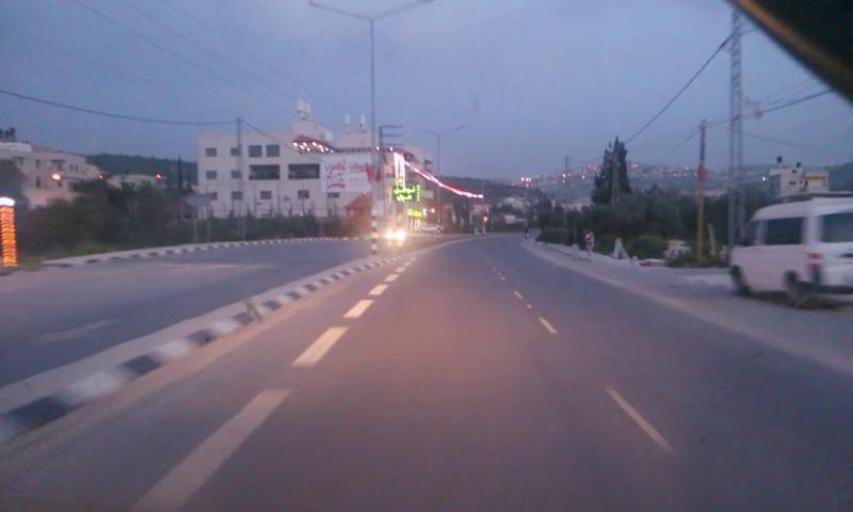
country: PS
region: West Bank
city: Dayr Sharaf
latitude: 32.2507
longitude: 35.1888
